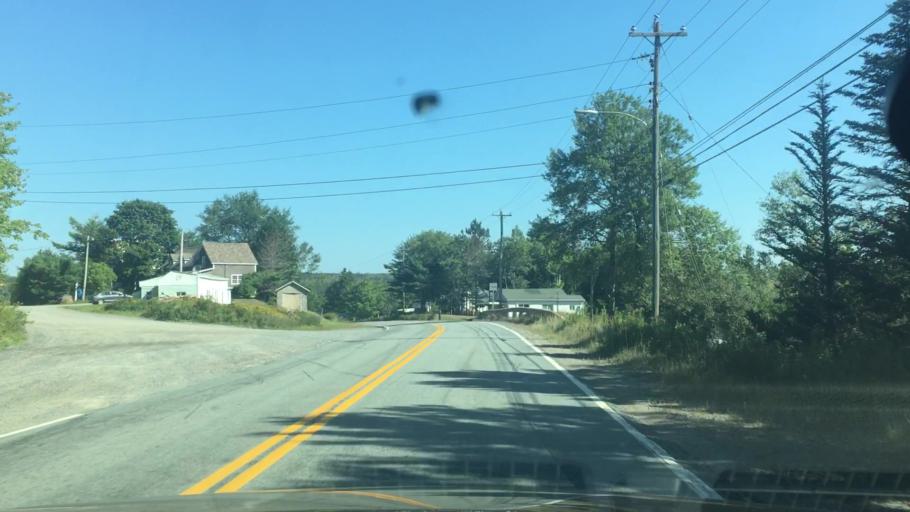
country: CA
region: Nova Scotia
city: New Glasgow
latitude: 44.9133
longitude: -62.5397
